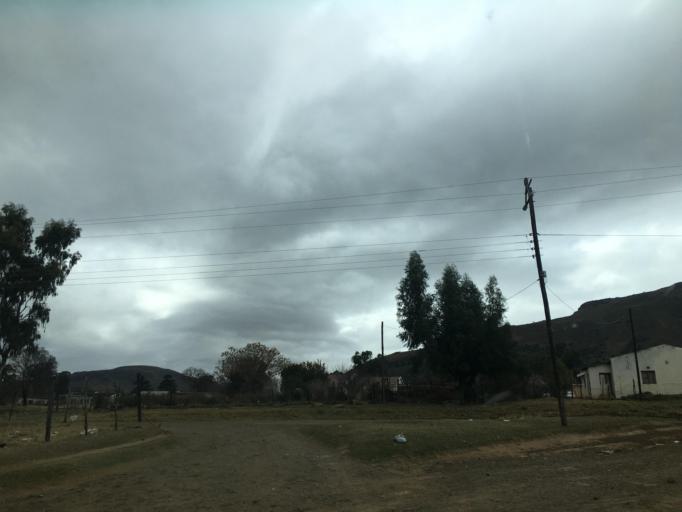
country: ZA
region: Eastern Cape
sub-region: Chris Hani District Municipality
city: Cala
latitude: -31.5314
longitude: 27.7013
